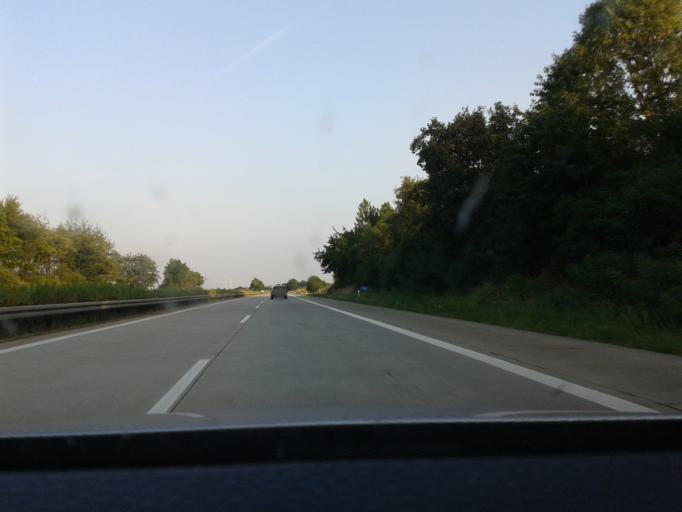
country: DE
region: Saxony
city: Grossweitzschen
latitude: 51.1805
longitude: 13.0280
